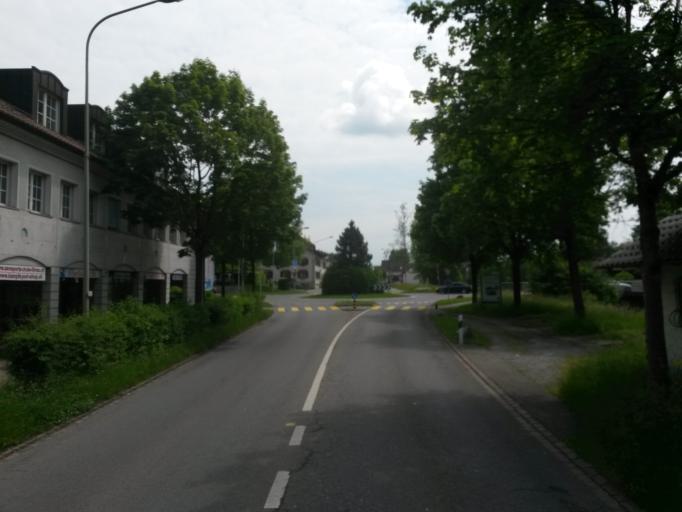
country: CH
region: Zurich
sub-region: Bezirk Pfaeffikon
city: Illnau / Unter-Illnau
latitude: 47.4091
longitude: 8.7255
